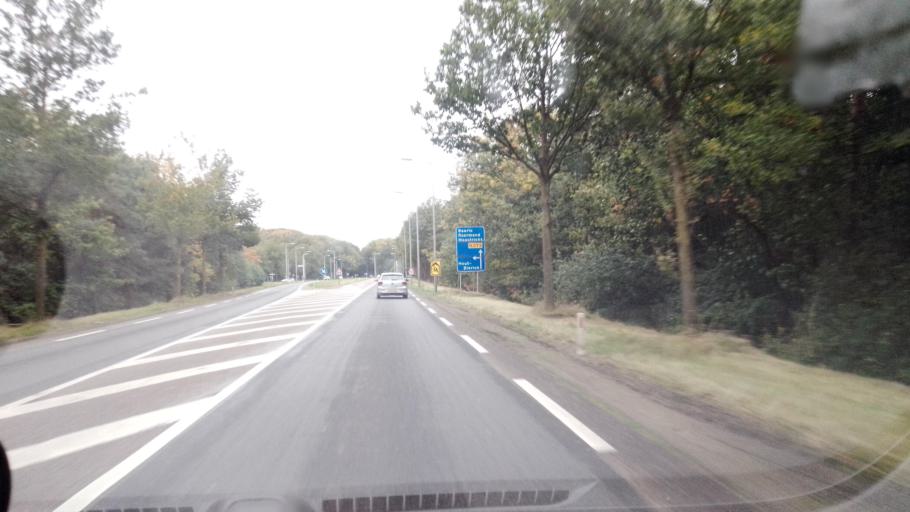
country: NL
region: Limburg
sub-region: Gemeente Venlo
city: Tegelen
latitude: 51.3521
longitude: 6.1140
